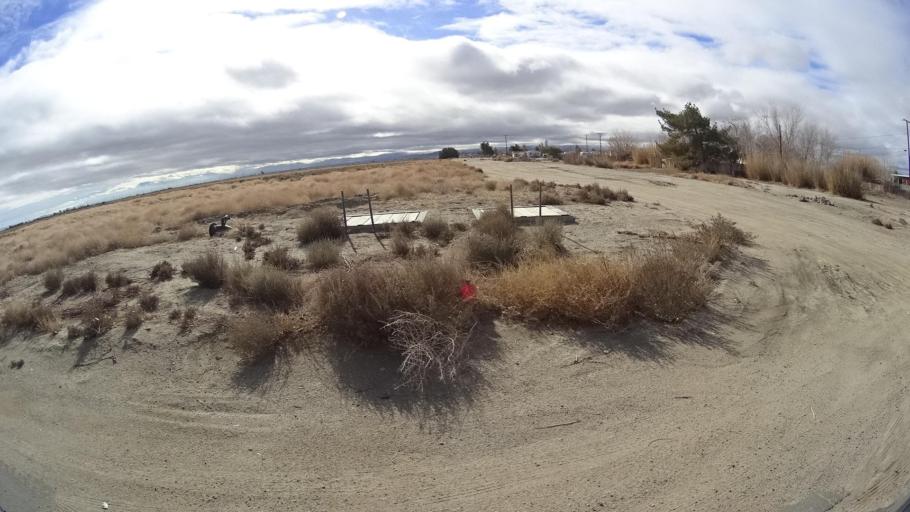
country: US
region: California
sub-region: Kern County
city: Rosamond
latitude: 34.8346
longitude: -118.2466
